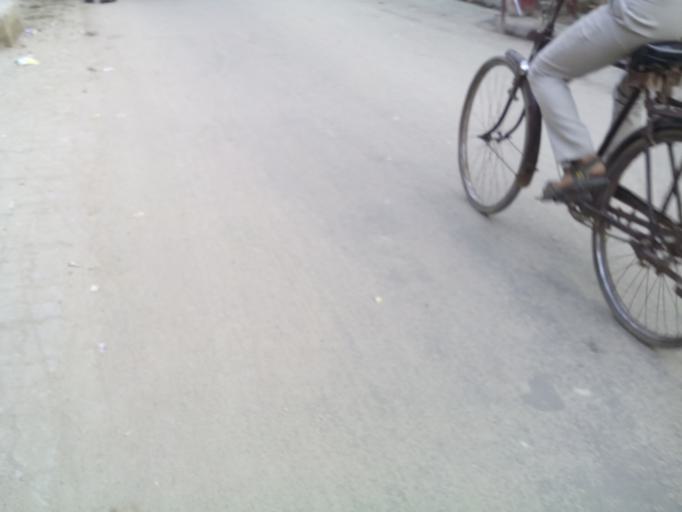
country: IN
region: Uttar Pradesh
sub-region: Kanpur
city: Kanpur
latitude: 26.4339
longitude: 80.3017
